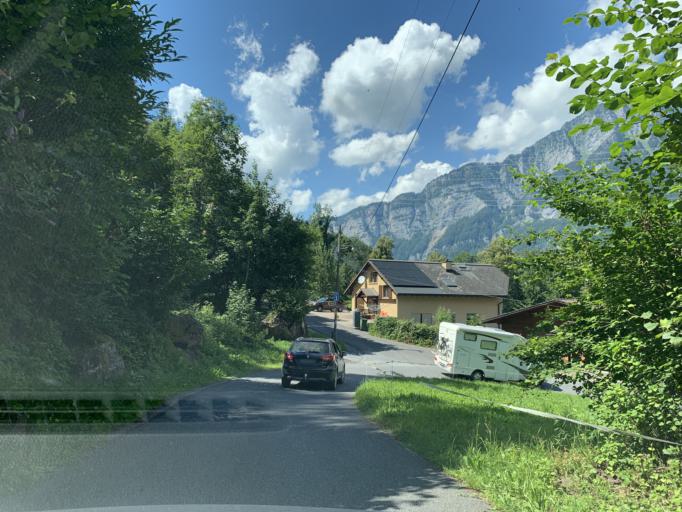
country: CH
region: Saint Gallen
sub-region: Wahlkreis Sarganserland
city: Quarten
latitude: 47.1090
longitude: 9.2126
